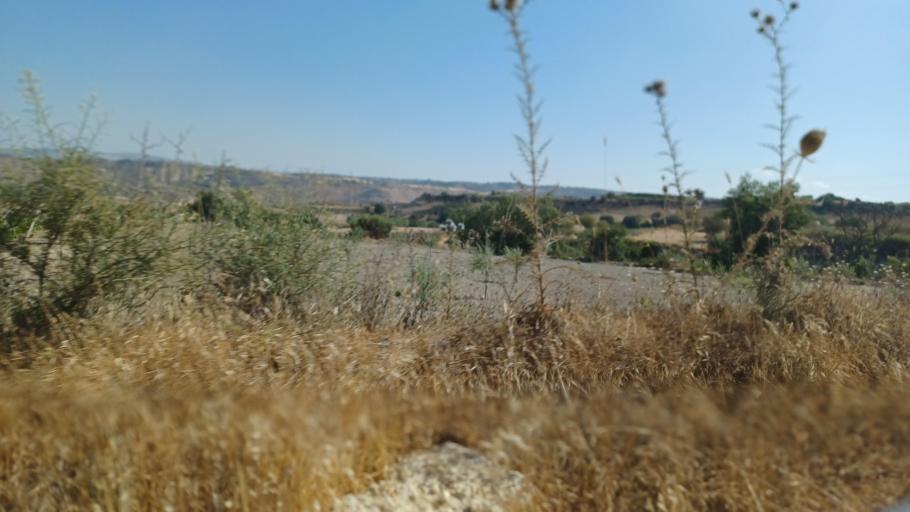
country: CY
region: Pafos
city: Tala
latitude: 34.9023
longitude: 32.4894
